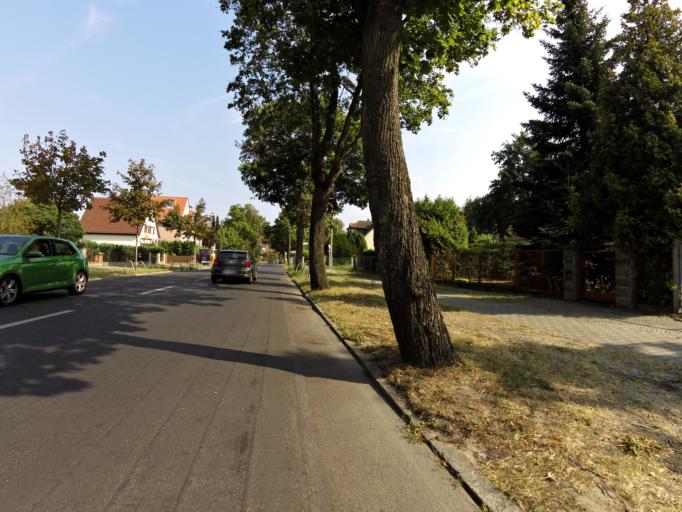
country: DE
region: Berlin
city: Grunau
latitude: 52.4158
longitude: 13.5586
